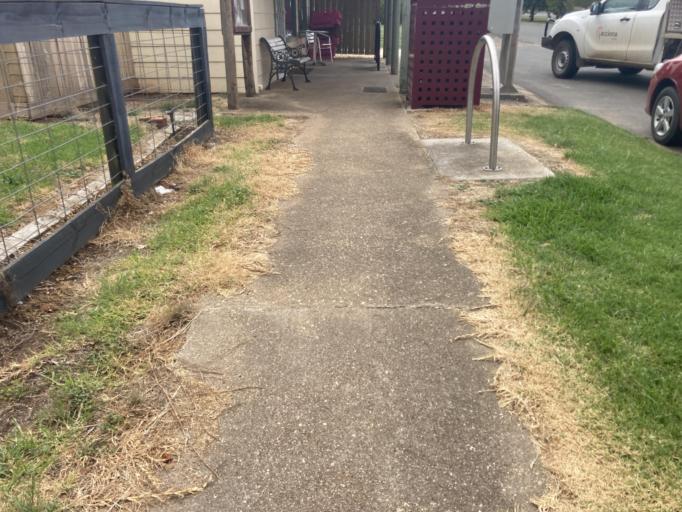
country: AU
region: Victoria
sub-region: Ballarat North
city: Newington
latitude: -37.3568
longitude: 143.6363
